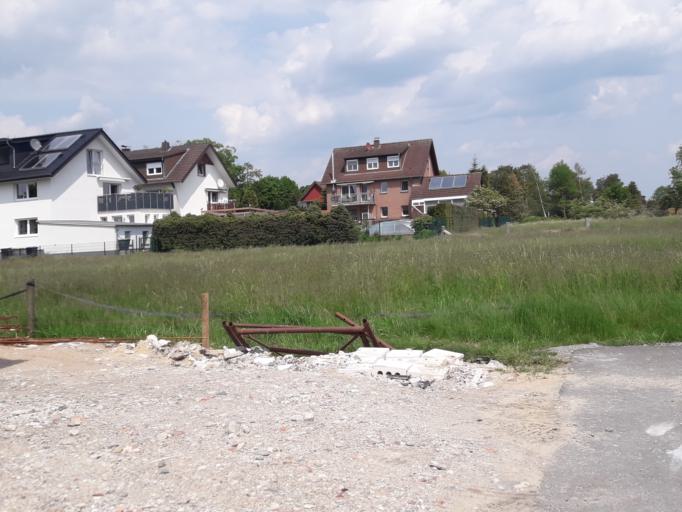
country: DE
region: North Rhine-Westphalia
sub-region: Regierungsbezirk Detmold
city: Paderborn
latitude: 51.7558
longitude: 8.7377
